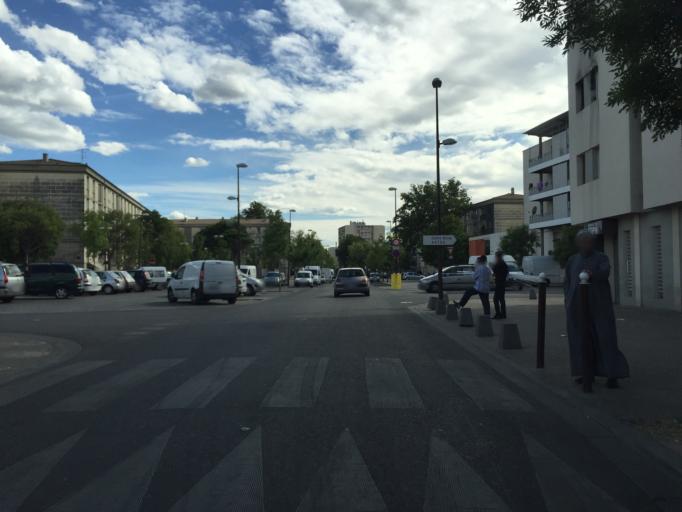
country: FR
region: Provence-Alpes-Cote d'Azur
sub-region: Departement du Vaucluse
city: Avignon
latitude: 43.9314
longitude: 4.8011
